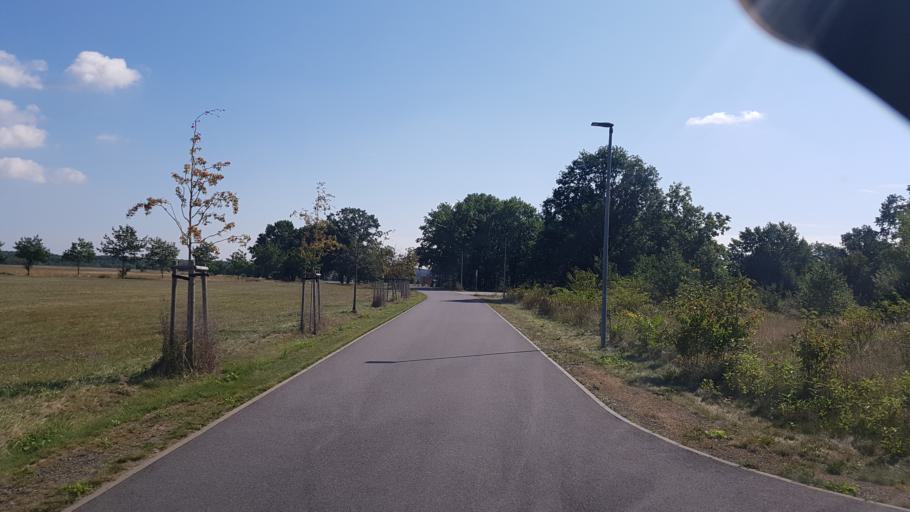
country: DE
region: Brandenburg
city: Vetschau
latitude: 51.7106
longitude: 14.0916
